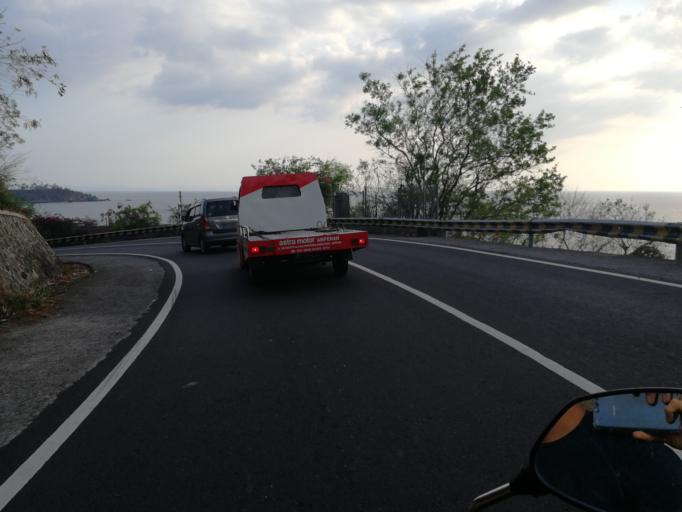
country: ID
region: West Nusa Tenggara
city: Karangsubagan
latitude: -8.4702
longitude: 116.0370
